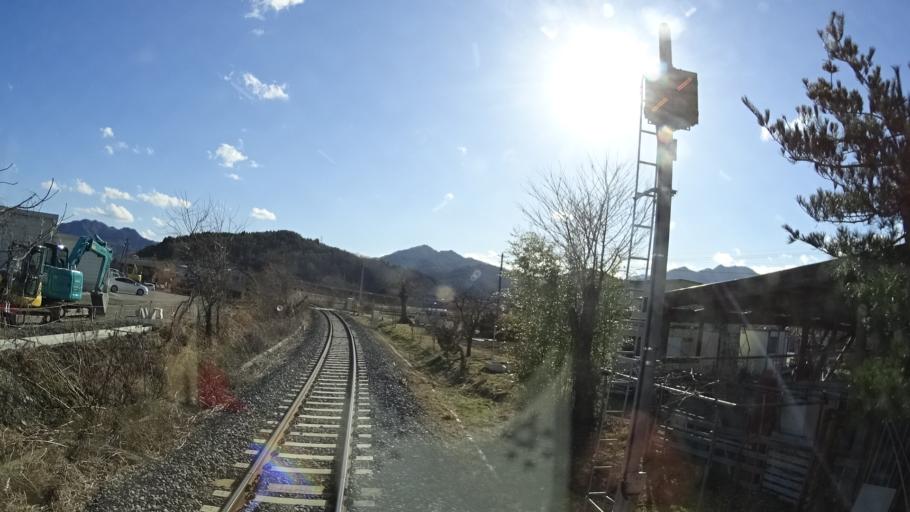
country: JP
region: Iwate
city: Yamada
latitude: 39.5400
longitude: 141.9267
